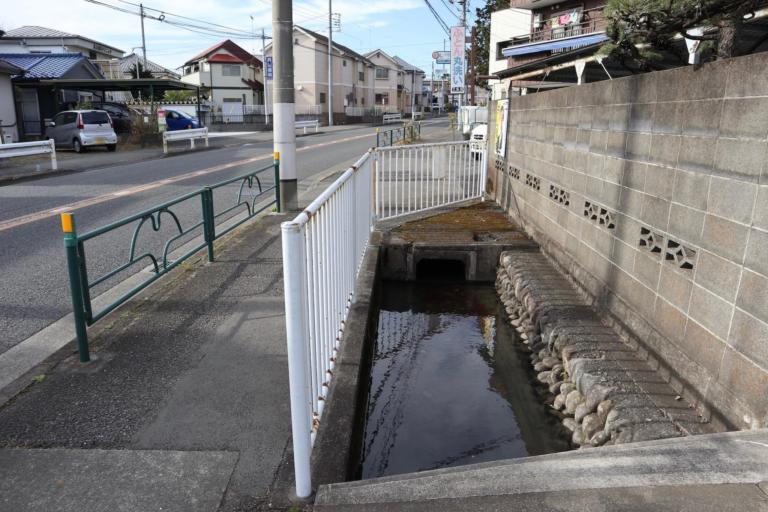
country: JP
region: Tokyo
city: Fussa
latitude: 35.7049
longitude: 139.3451
